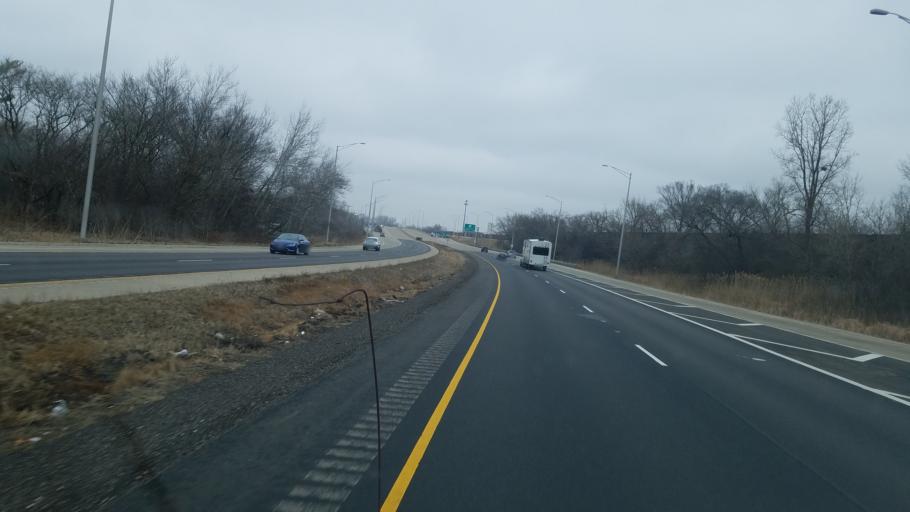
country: US
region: Illinois
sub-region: Lake County
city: Gurnee
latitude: 42.3652
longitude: -87.8947
